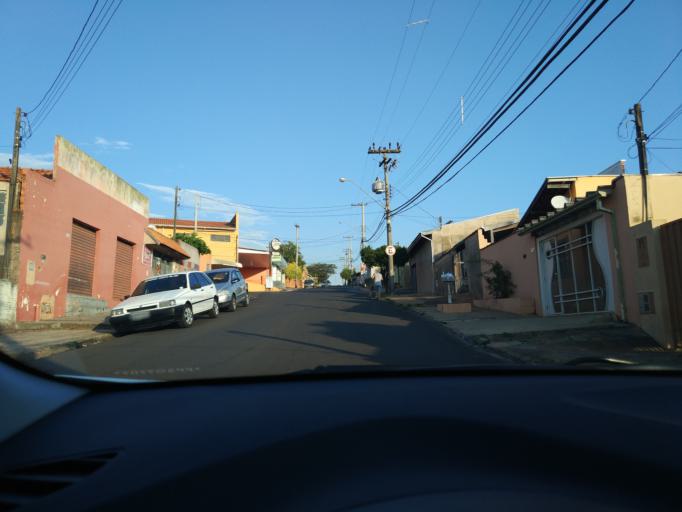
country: BR
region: Sao Paulo
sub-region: Botucatu
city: Botucatu
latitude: -22.8992
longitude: -48.4303
